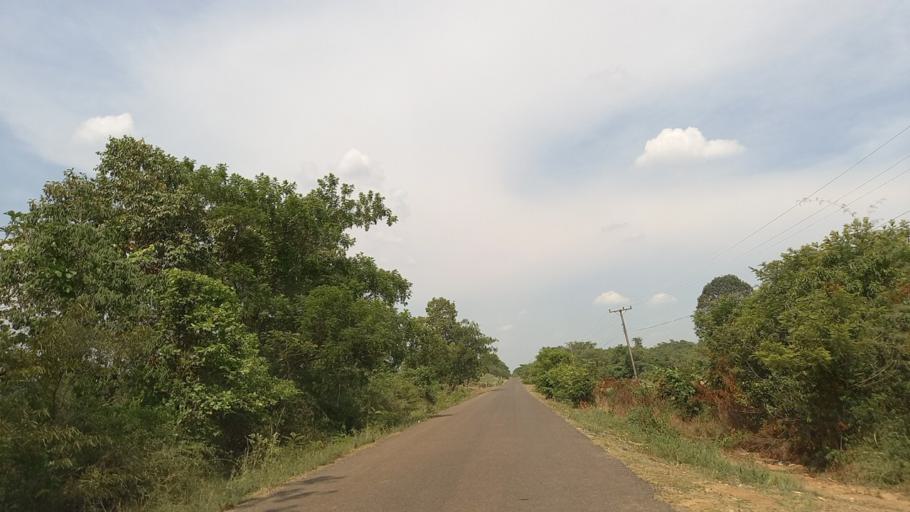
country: LA
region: Bolikhamxai
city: Muang Pakxan
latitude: 18.4290
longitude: 103.7257
